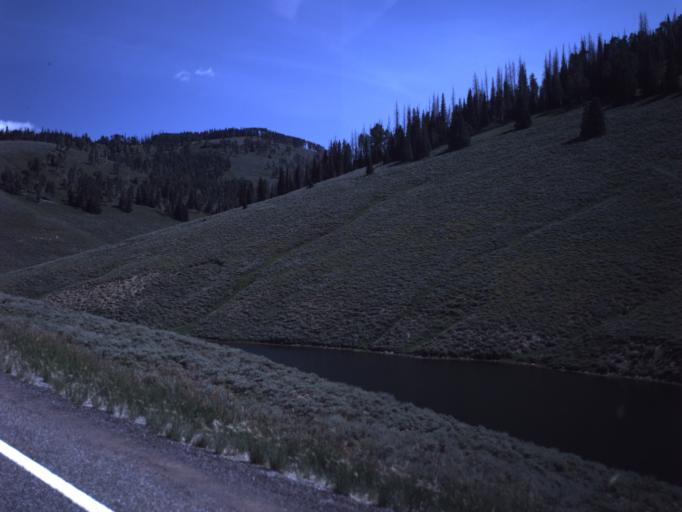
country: US
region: Utah
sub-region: Sanpete County
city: Fairview
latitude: 39.6443
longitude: -111.2384
